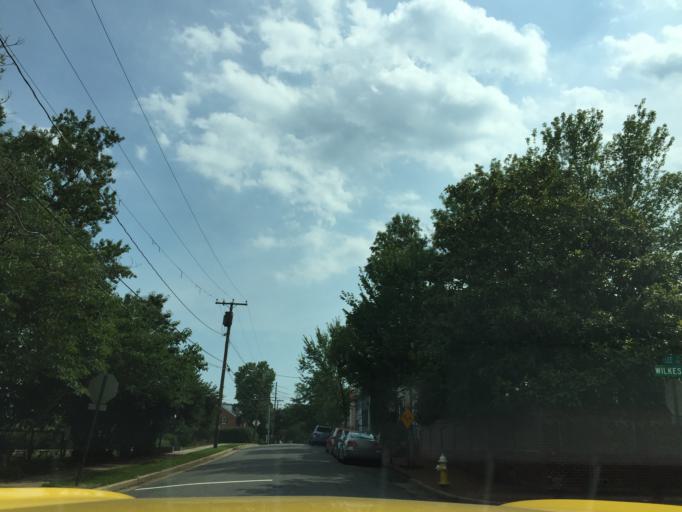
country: US
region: Virginia
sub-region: City of Alexandria
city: Alexandria
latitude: 38.7999
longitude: -77.0424
